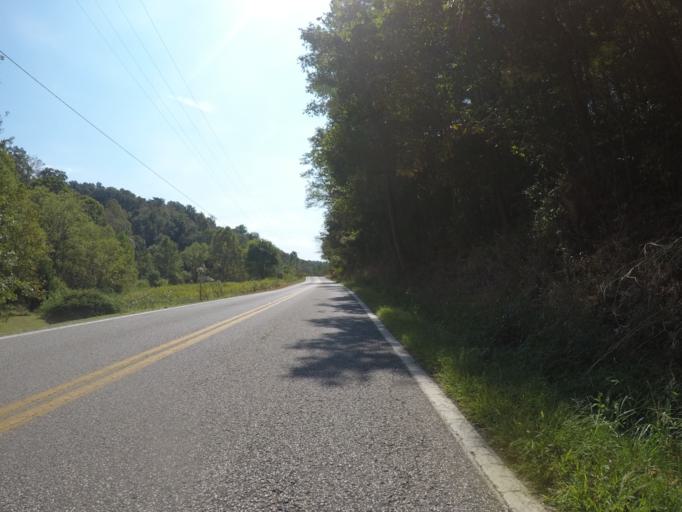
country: US
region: West Virginia
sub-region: Cabell County
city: Lesage
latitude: 38.5657
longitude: -82.3975
